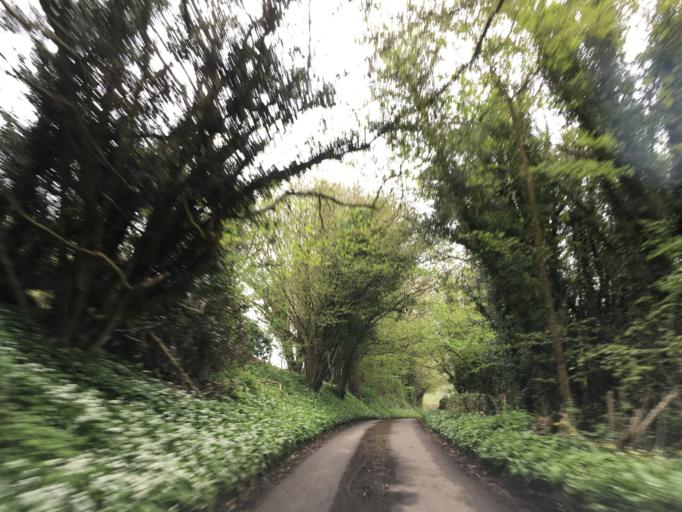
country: GB
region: England
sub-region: Gloucestershire
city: Wotton-under-Edge
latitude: 51.6260
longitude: -2.3154
